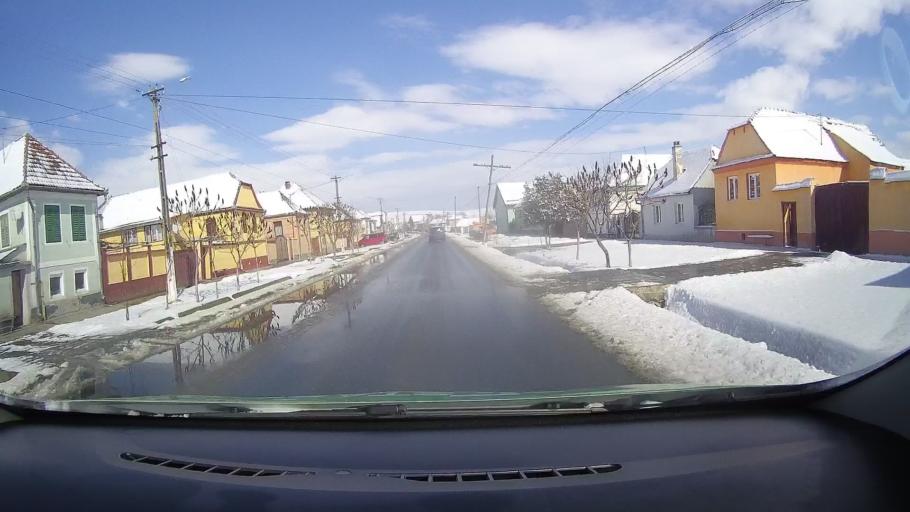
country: RO
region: Sibiu
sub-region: Comuna Nocrich
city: Nocrich
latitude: 45.8982
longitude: 24.4574
